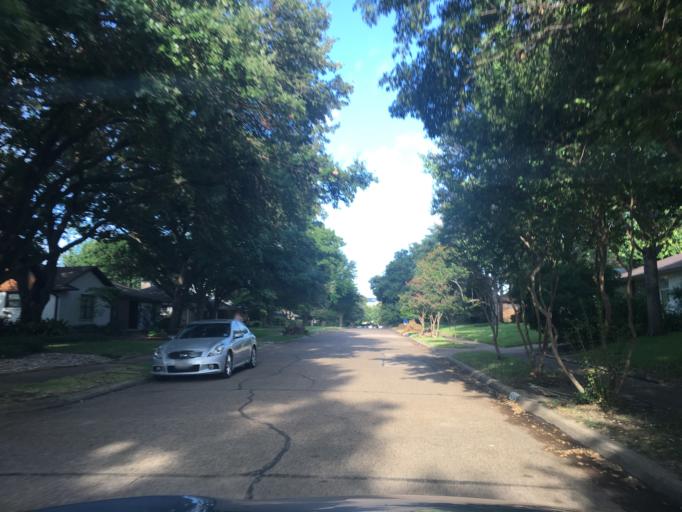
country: US
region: Texas
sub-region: Dallas County
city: Highland Park
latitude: 32.8436
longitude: -96.7572
